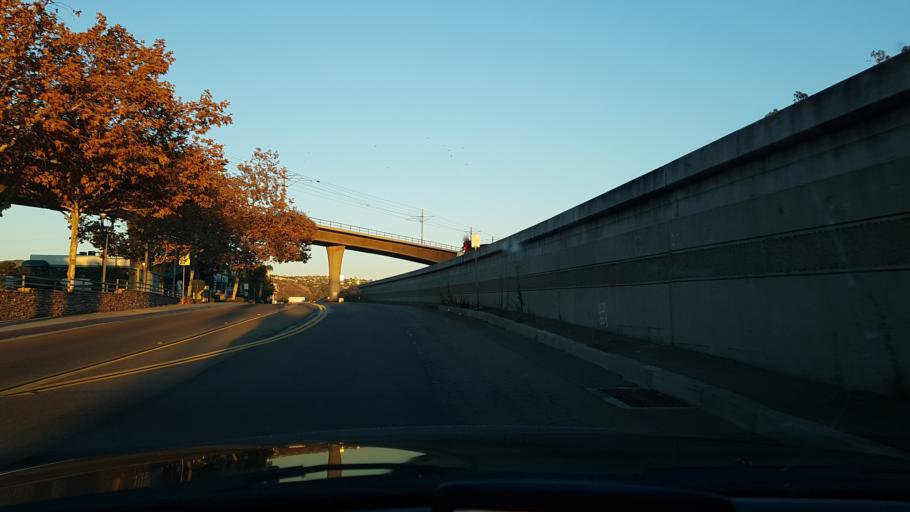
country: US
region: California
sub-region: San Diego County
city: La Mesa
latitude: 32.7800
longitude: -117.0980
